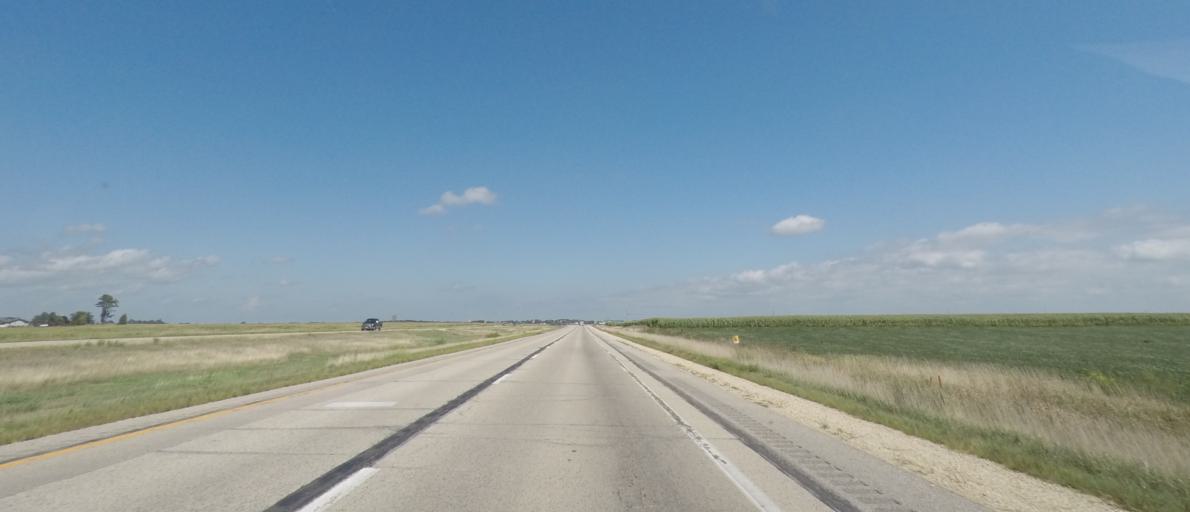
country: US
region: Iowa
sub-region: Linn County
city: Springville
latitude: 42.0696
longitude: -91.3698
